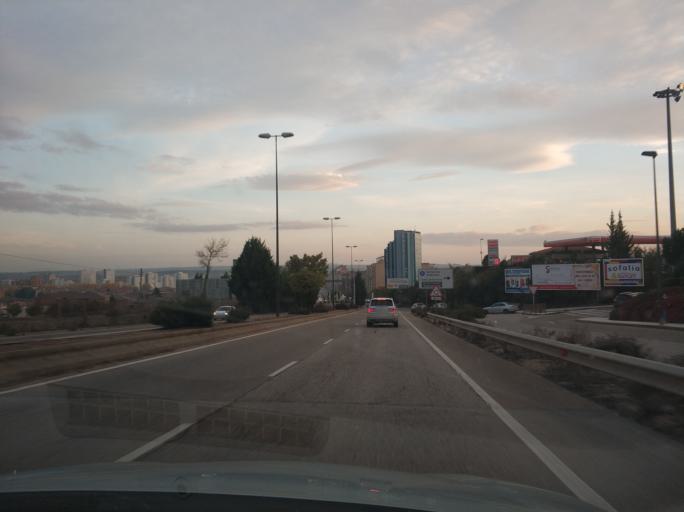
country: ES
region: Castille and Leon
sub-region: Provincia de Burgos
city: Burgos
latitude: 42.3593
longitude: -3.6940
